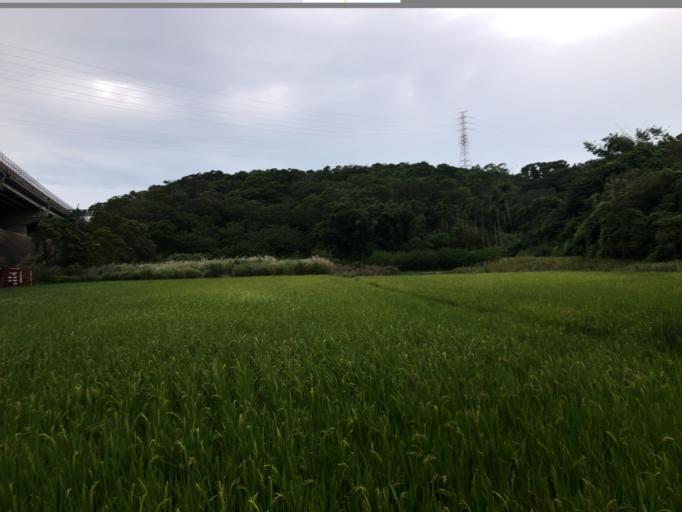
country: TW
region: Taiwan
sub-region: Hsinchu
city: Hsinchu
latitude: 24.7536
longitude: 120.9480
